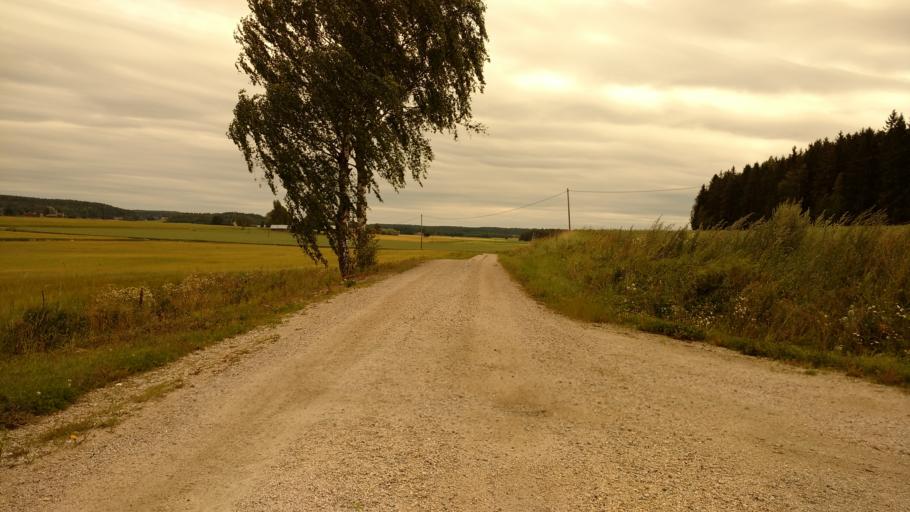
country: FI
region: Varsinais-Suomi
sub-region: Turku
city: Paimio
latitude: 60.4172
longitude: 22.8337
